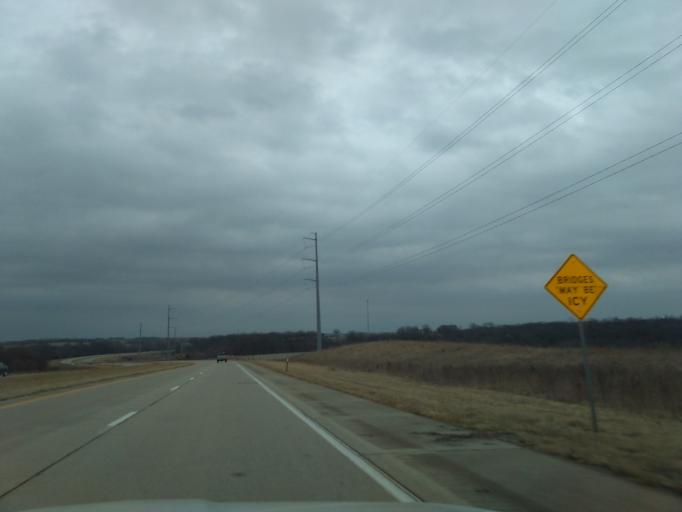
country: US
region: Nebraska
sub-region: Otoe County
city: Syracuse
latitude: 40.6755
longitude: -96.0463
